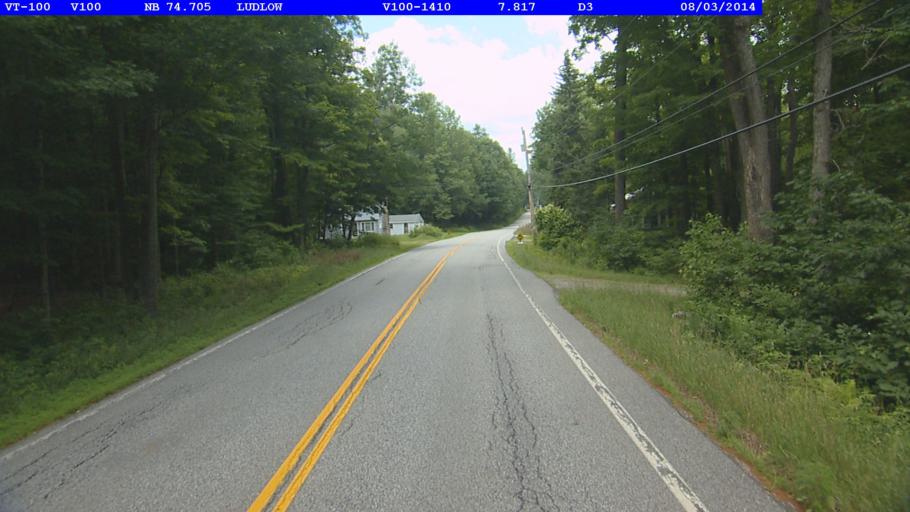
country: US
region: Vermont
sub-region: Windsor County
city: Chester
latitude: 43.4554
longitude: -72.7076
